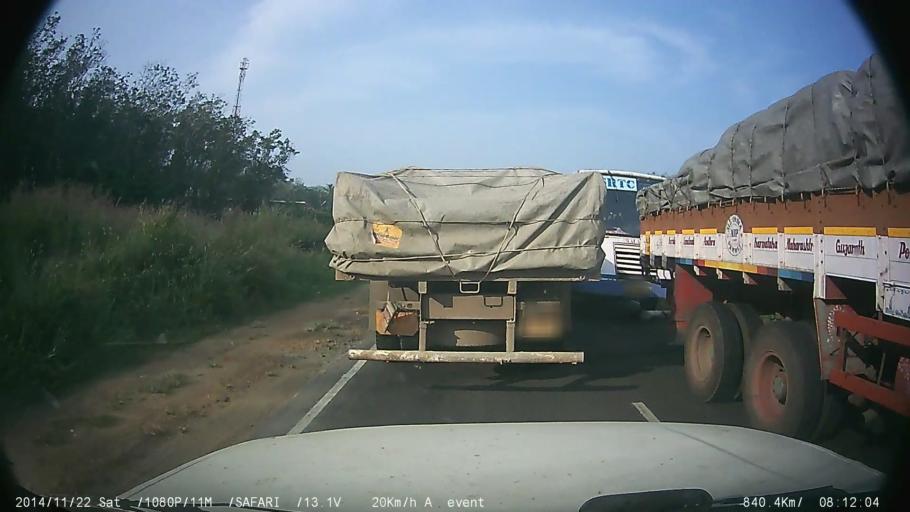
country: IN
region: Kerala
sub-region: Thrissur District
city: Chelakara
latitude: 10.5842
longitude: 76.4329
